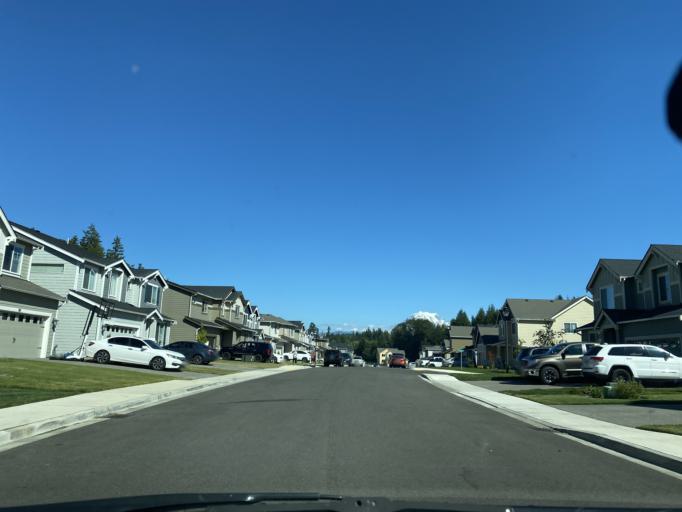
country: US
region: Washington
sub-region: Pierce County
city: Graham
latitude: 47.0870
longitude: -122.2601
